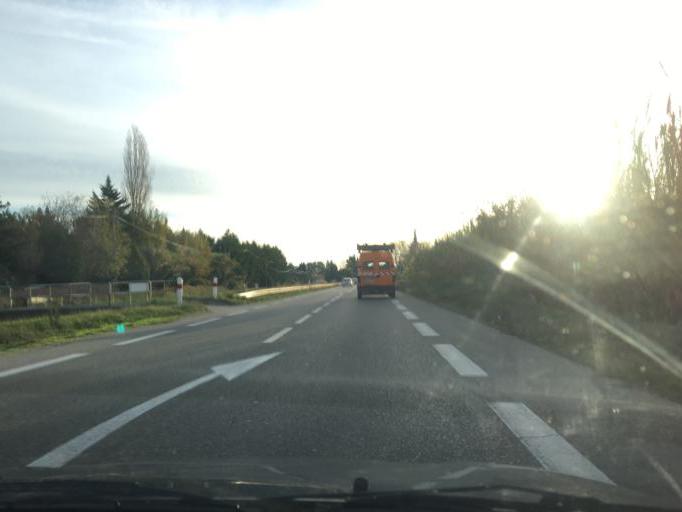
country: FR
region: Provence-Alpes-Cote d'Azur
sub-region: Departement des Bouches-du-Rhone
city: Mallemort
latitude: 43.7571
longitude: 5.1471
